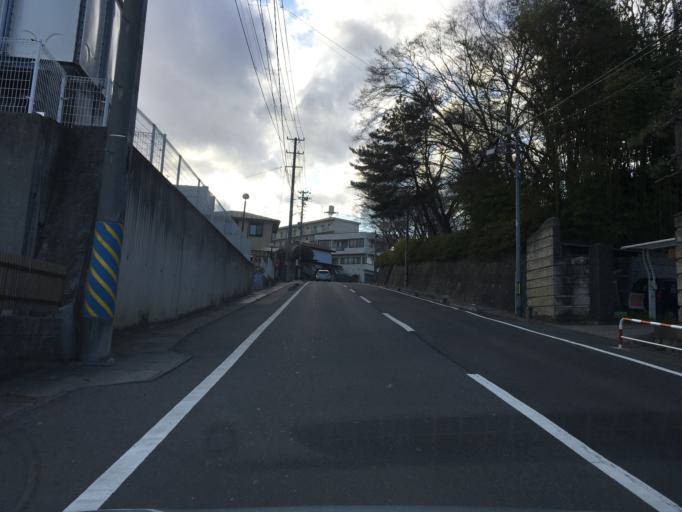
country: JP
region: Miyagi
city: Ishinomaki
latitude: 38.4297
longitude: 141.3030
